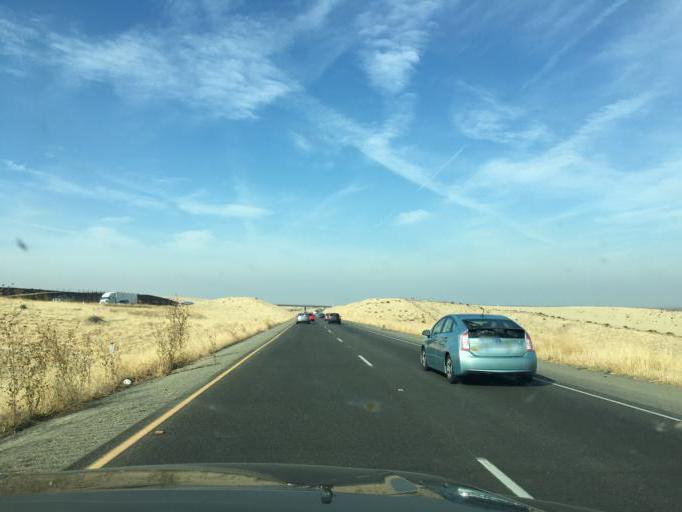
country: US
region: California
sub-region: Fresno County
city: Coalinga
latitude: 36.3249
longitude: -120.2947
